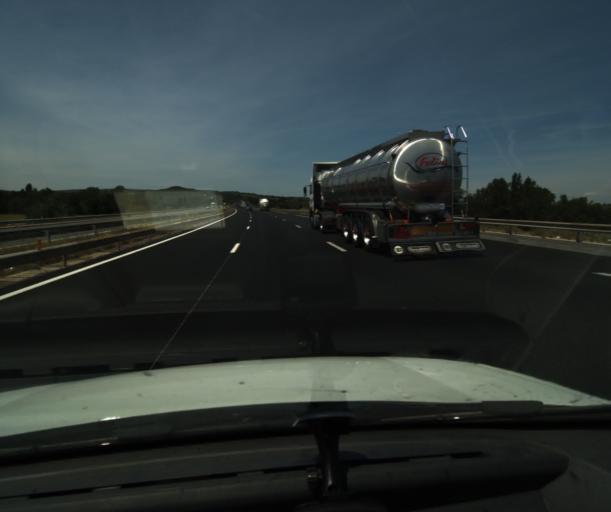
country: FR
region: Languedoc-Roussillon
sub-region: Departement de l'Aude
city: Sigean
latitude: 43.0414
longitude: 2.9494
